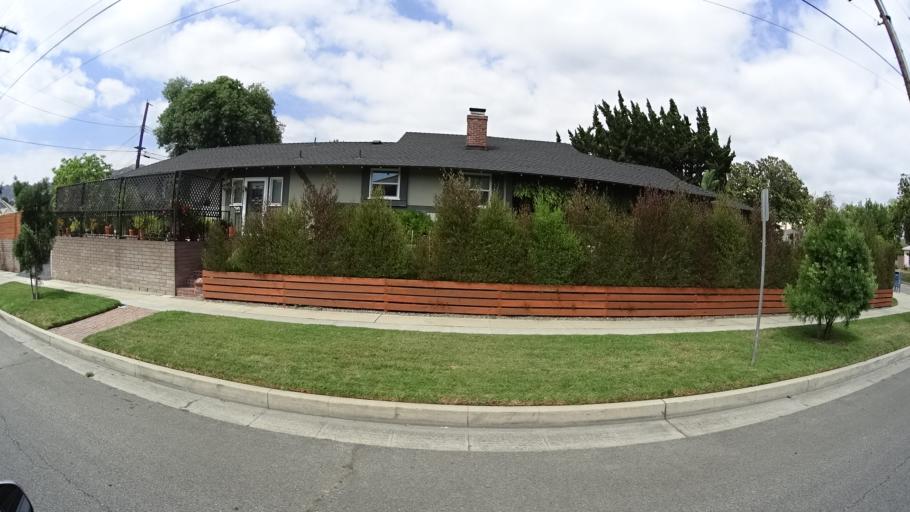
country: US
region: California
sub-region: Los Angeles County
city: Burbank
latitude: 34.1942
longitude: -118.3213
